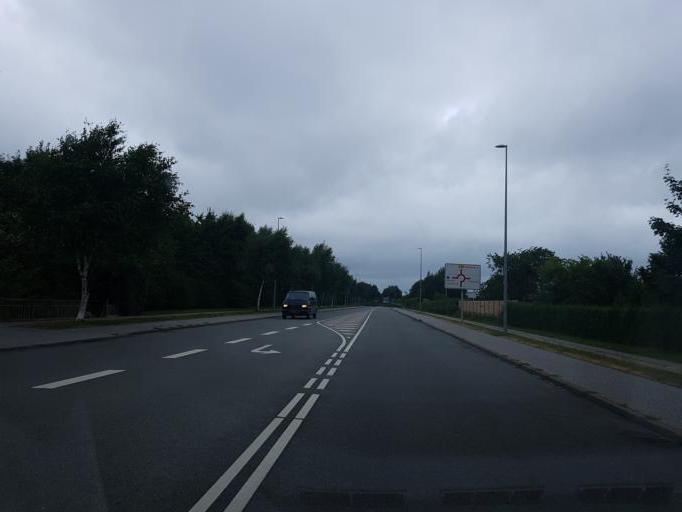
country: DK
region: South Denmark
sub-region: Varde Kommune
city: Varde
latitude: 55.6326
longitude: 8.4844
